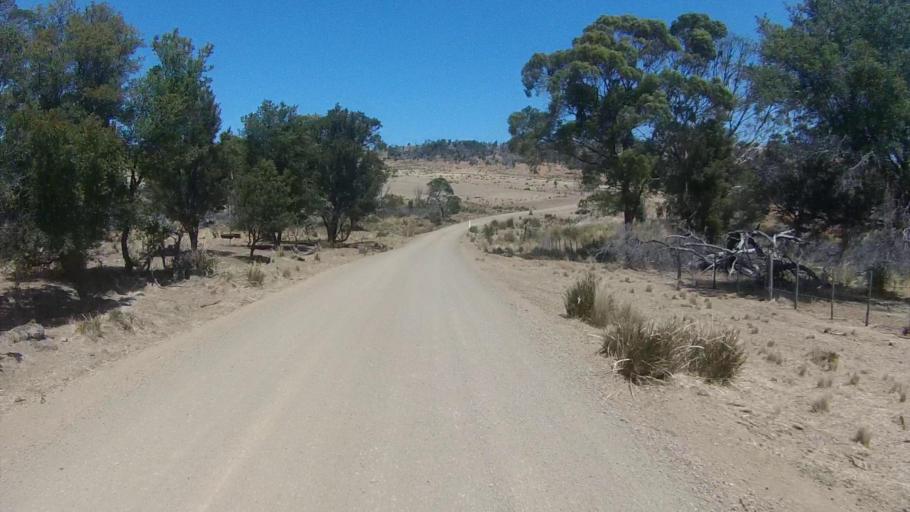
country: AU
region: Tasmania
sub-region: Sorell
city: Sorell
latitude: -42.8950
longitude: 147.8405
